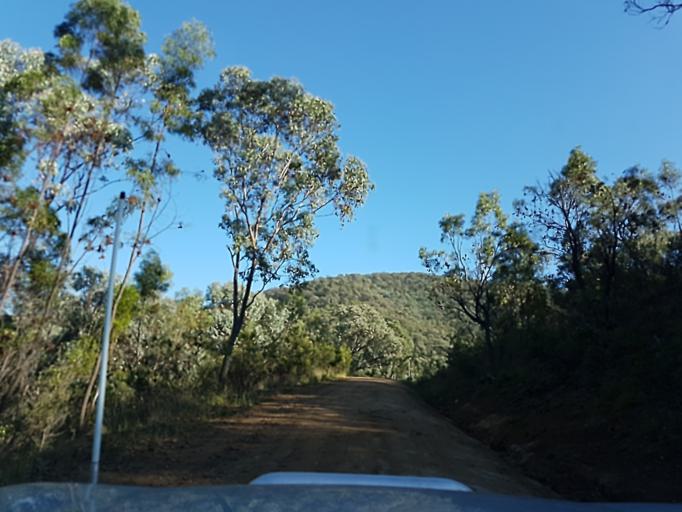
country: AU
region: New South Wales
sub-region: Snowy River
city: Jindabyne
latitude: -36.9355
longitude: 148.3398
